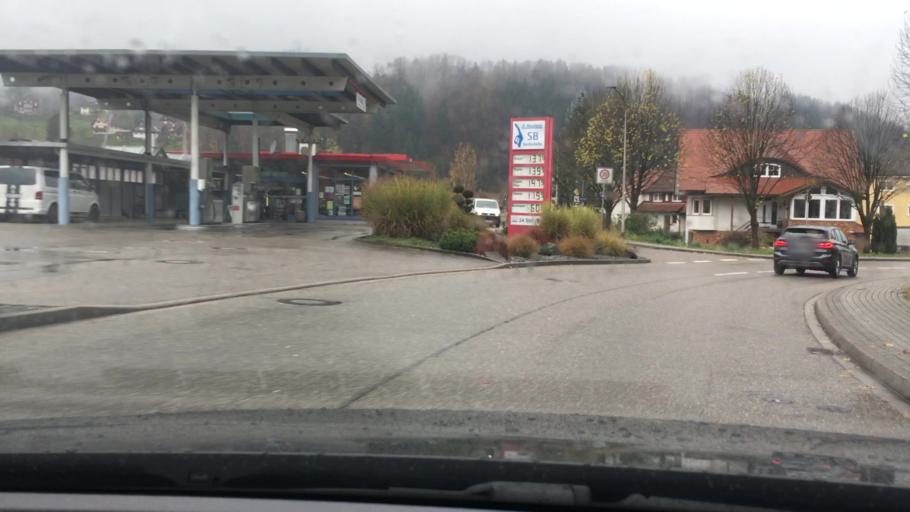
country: DE
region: Baden-Wuerttemberg
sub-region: Freiburg Region
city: Oppenau
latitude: 48.4733
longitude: 8.1570
